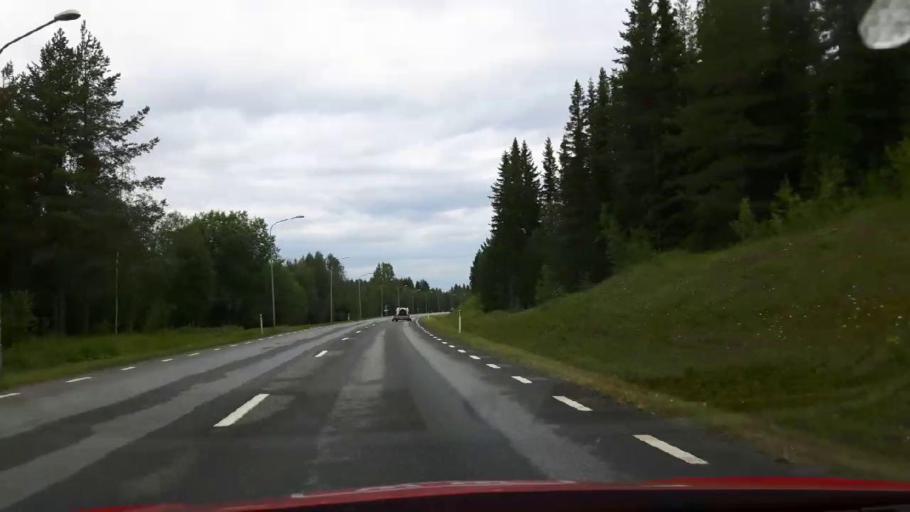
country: SE
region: Jaemtland
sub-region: Stroemsunds Kommun
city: Stroemsund
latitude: 63.6695
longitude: 15.3915
